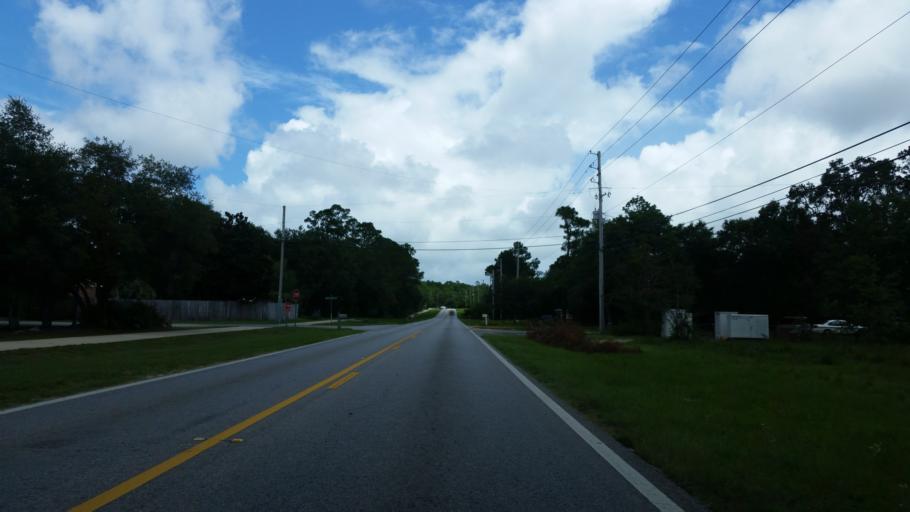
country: US
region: Florida
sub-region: Santa Rosa County
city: Holley
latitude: 30.4391
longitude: -86.9199
